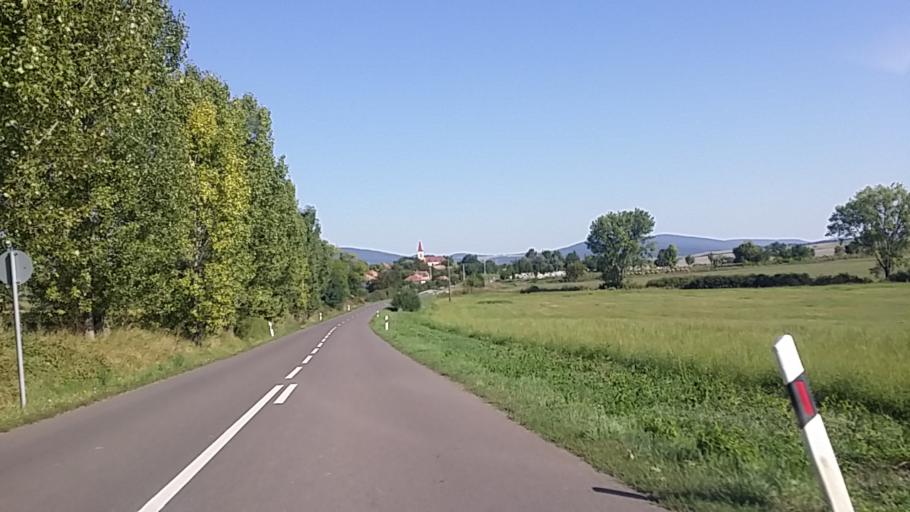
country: HU
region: Nograd
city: Jobbagyi
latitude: 47.8572
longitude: 19.6267
